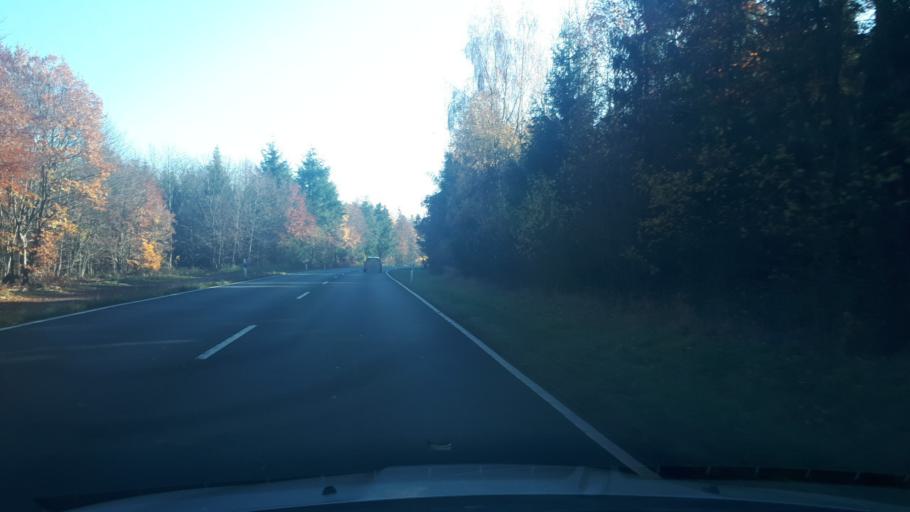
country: DE
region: Rheinland-Pfalz
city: Buchel
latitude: 50.1658
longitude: 7.0976
